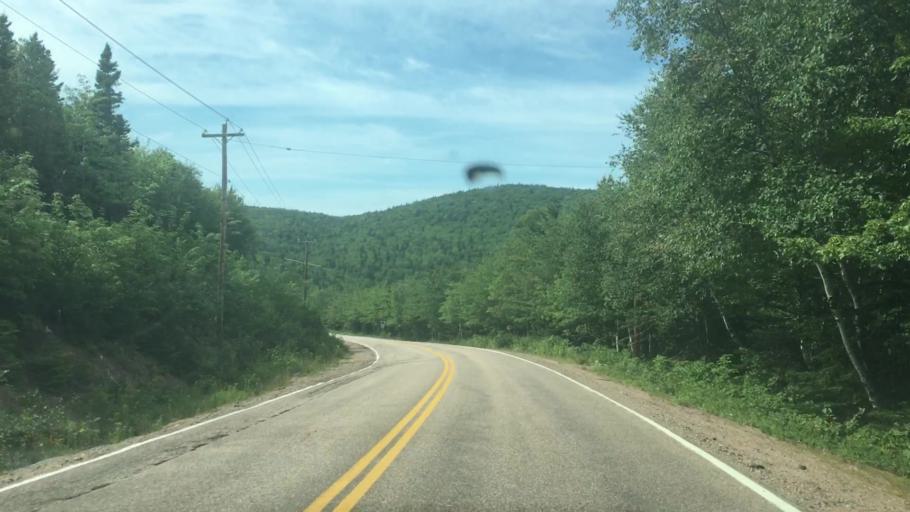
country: CA
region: Nova Scotia
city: Sydney Mines
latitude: 46.6057
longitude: -60.3914
